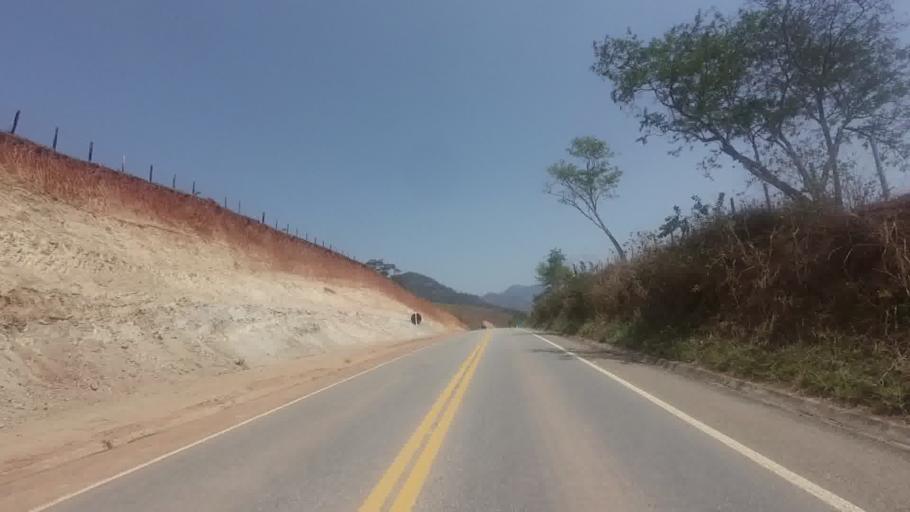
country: BR
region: Espirito Santo
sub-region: Jeronimo Monteiro
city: Jeronimo Monteiro
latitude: -20.8946
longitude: -41.2874
